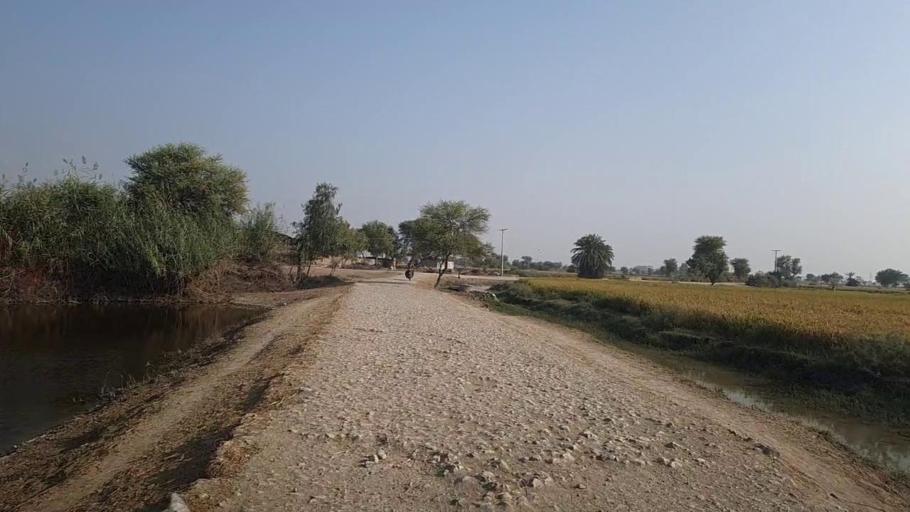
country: PK
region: Sindh
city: Kandhkot
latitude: 28.2877
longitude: 69.2574
